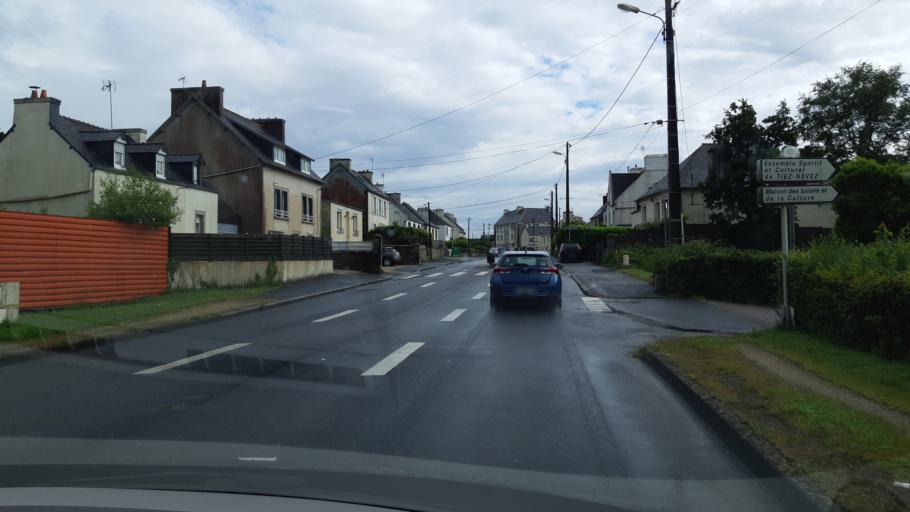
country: FR
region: Brittany
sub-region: Departement du Finistere
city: Landivisiau
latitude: 48.5165
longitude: -4.0719
